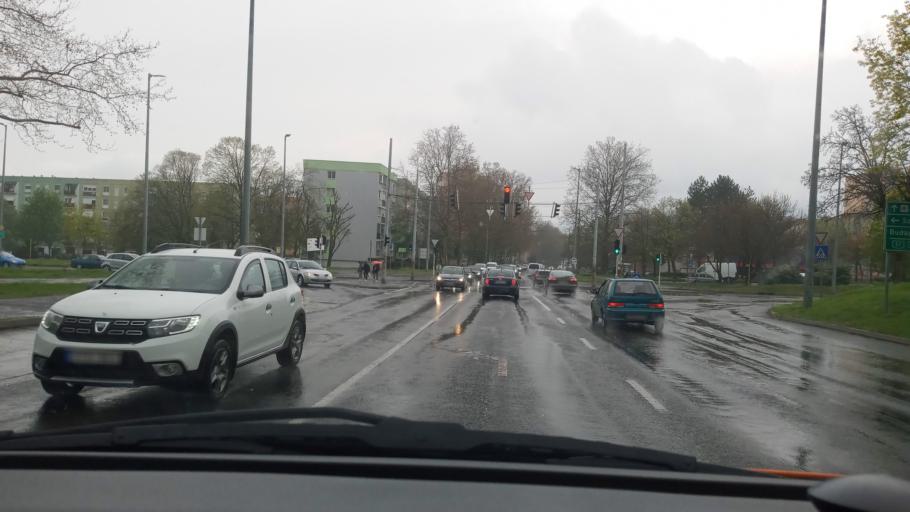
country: HU
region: Baranya
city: Pecs
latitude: 46.0419
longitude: 18.2162
